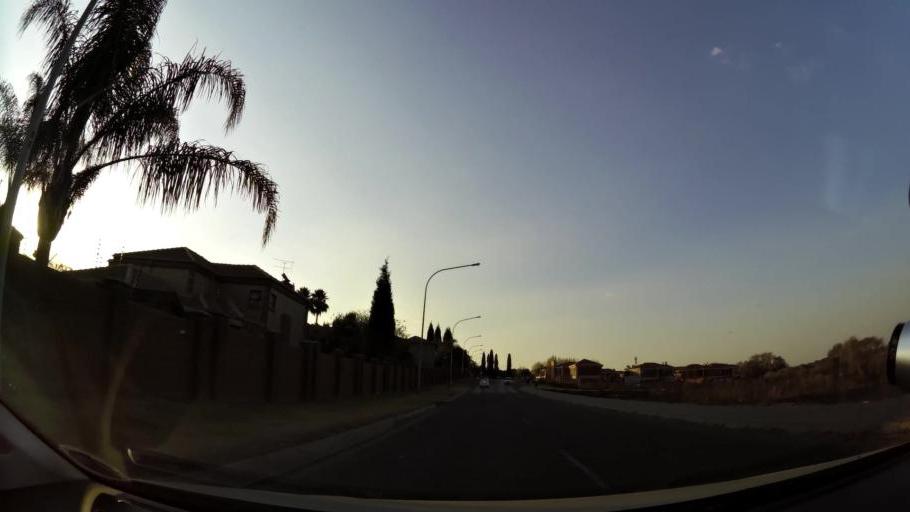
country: ZA
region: Gauteng
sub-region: City of Johannesburg Metropolitan Municipality
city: Modderfontein
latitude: -26.0849
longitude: 28.2187
